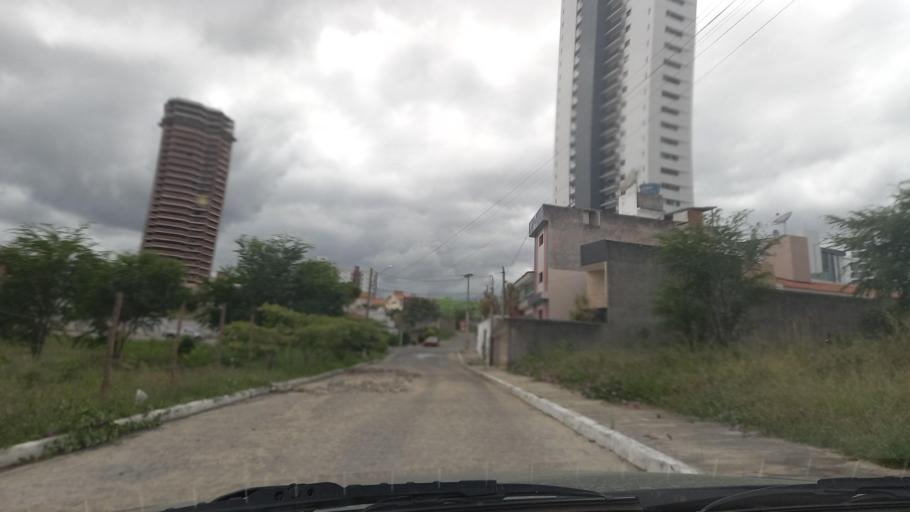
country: BR
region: Pernambuco
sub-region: Caruaru
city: Caruaru
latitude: -8.2667
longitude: -35.9672
